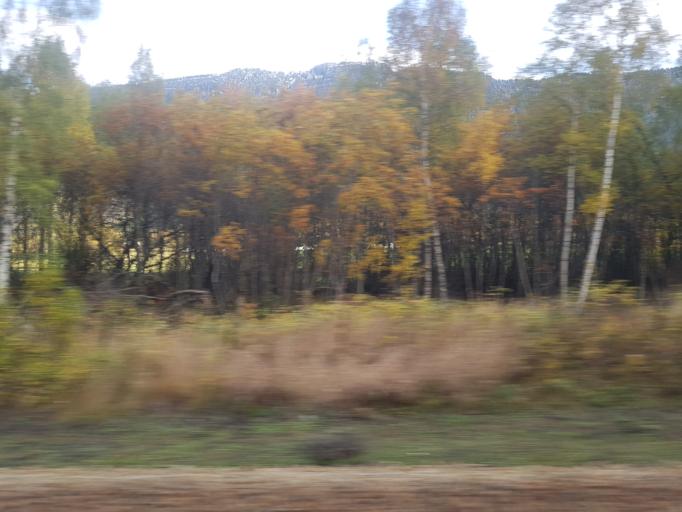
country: NO
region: Oppland
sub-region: Sel
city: Otta
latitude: 61.8365
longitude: 9.4808
